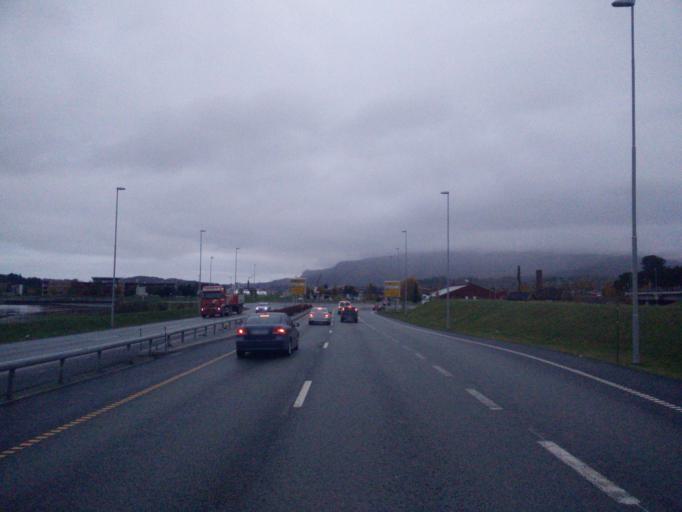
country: NO
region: Nord-Trondelag
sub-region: Stjordal
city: Stjordal
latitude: 63.4650
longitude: 10.9129
